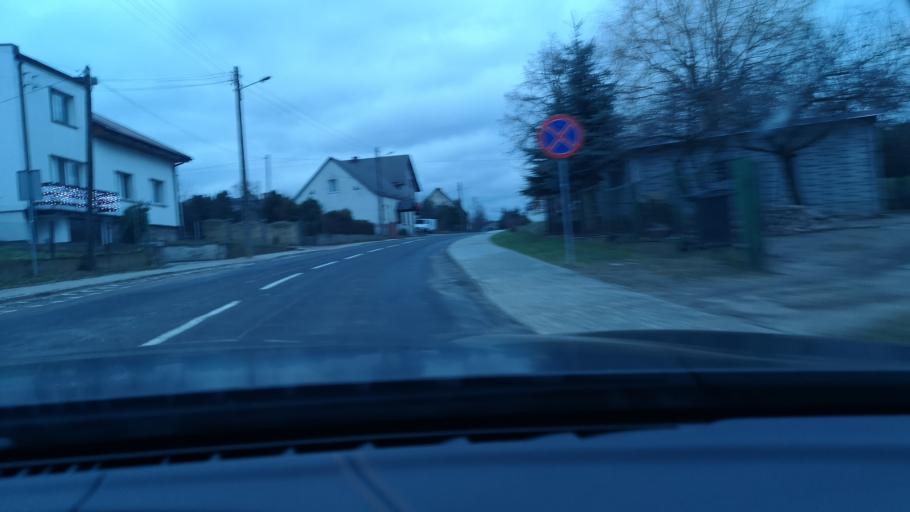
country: PL
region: Greater Poland Voivodeship
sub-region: Powiat slupecki
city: Orchowo
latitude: 52.5989
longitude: 18.0402
